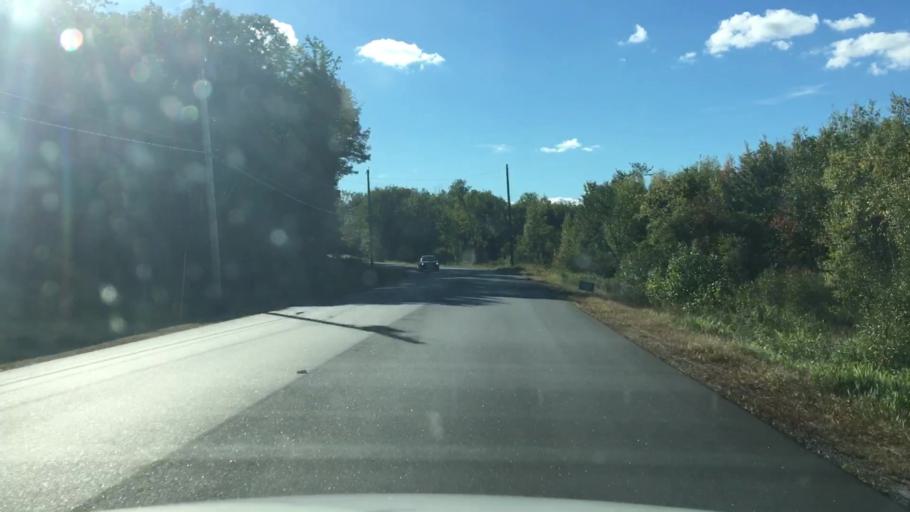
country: US
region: Maine
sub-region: Androscoggin County
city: Lisbon
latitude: 44.0729
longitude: -70.1299
